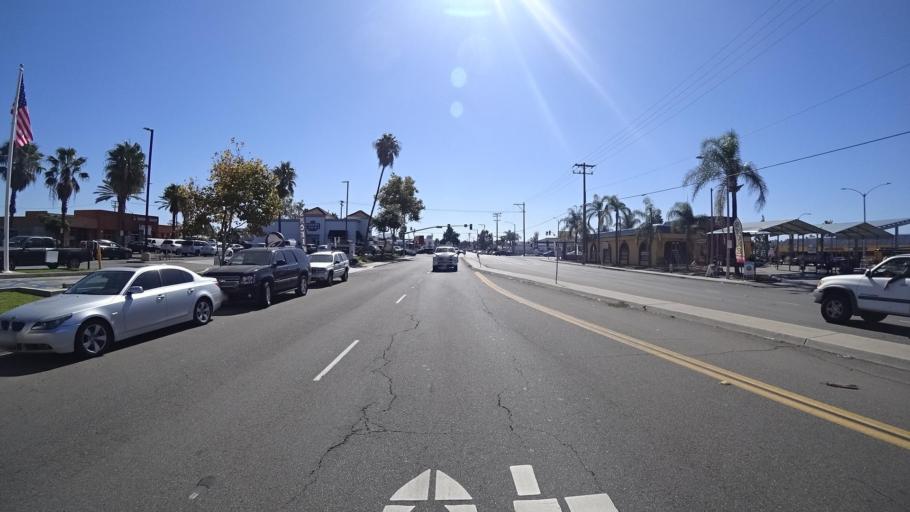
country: US
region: California
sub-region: San Diego County
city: Santee
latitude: 32.8200
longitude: -116.9623
